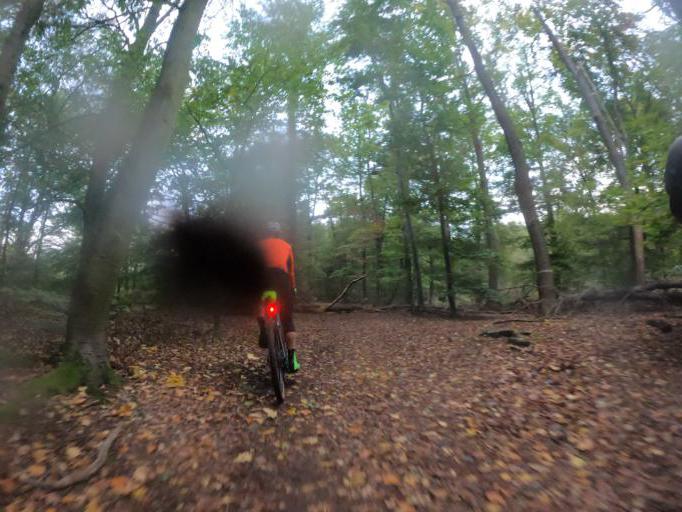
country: DE
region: Hesse
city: Langen
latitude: 50.0079
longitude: 8.6627
